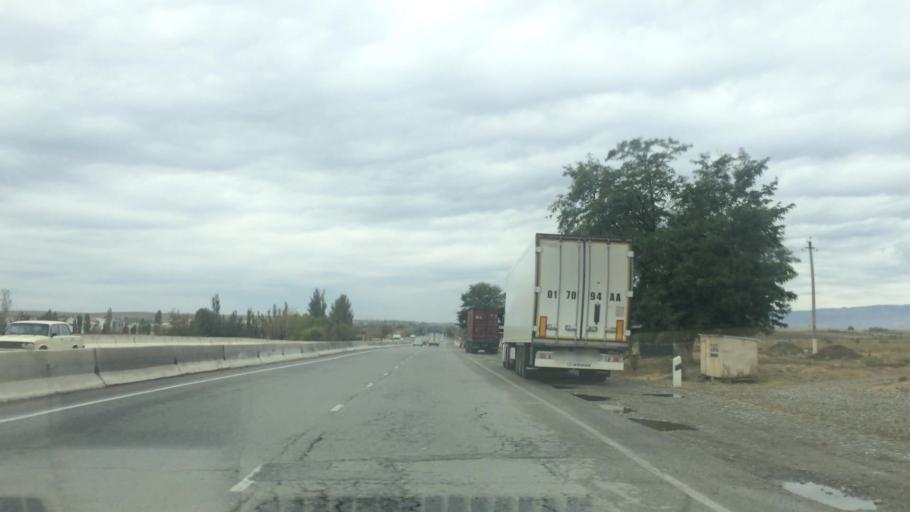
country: UZ
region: Jizzax
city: Jizzax
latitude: 39.9726
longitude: 67.5592
